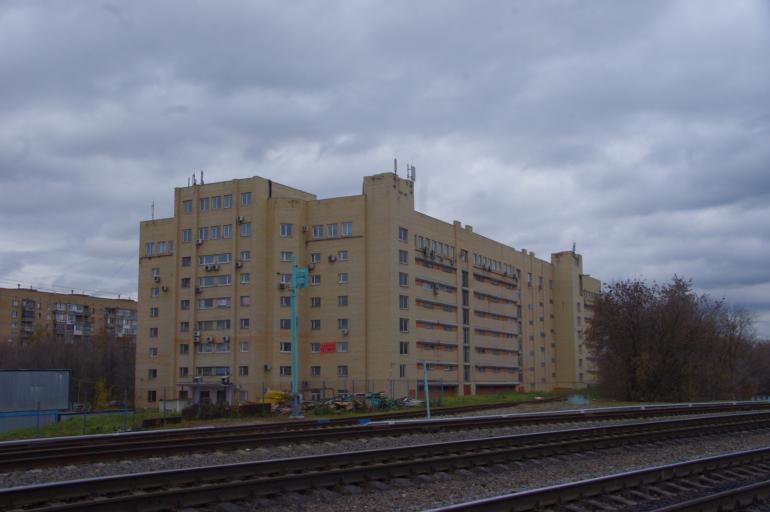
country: RU
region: Moscow
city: Sviblovo
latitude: 55.8456
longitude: 37.6386
